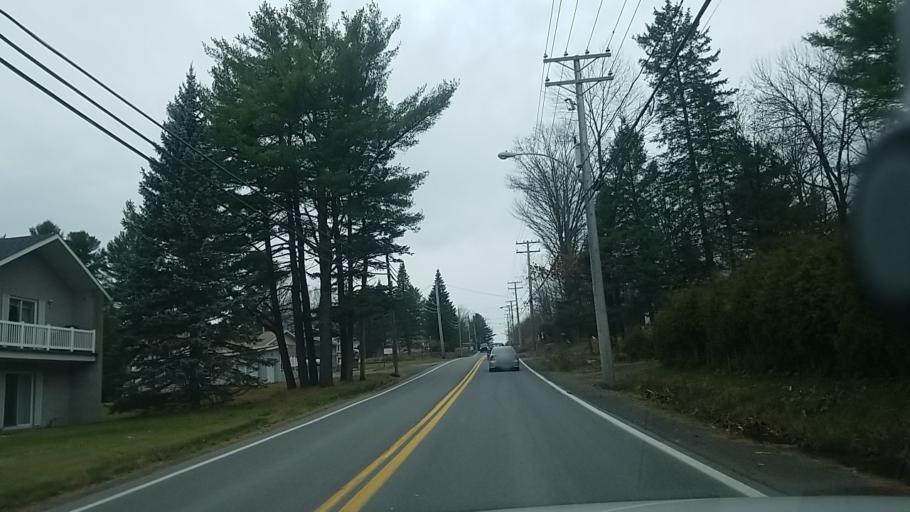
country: CA
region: Quebec
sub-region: Laurentides
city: Saint-Jerome
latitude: 45.7897
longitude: -74.0570
